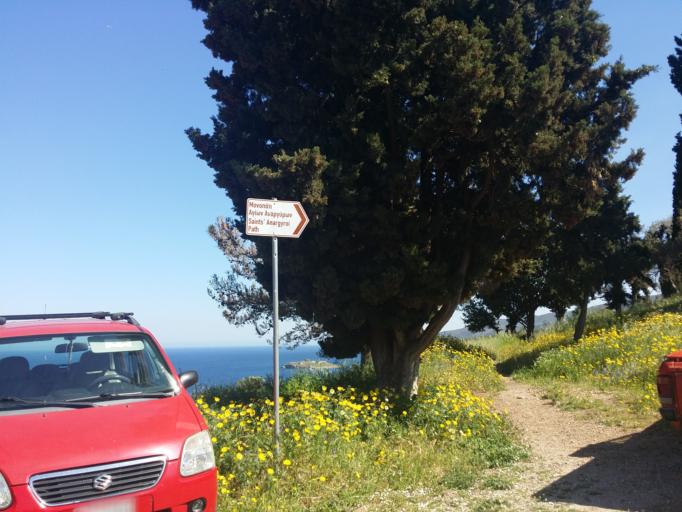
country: GR
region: Attica
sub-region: Nomos Piraios
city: Poros
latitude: 37.5003
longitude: 23.4583
